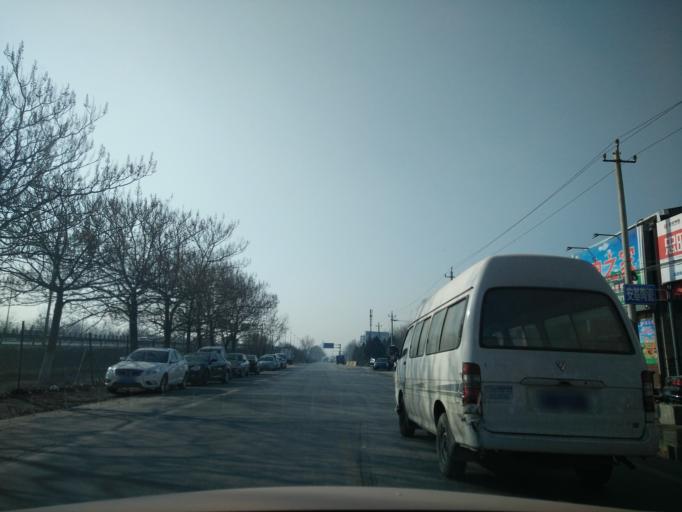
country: CN
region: Beijing
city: Jiugong
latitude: 39.8156
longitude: 116.4901
